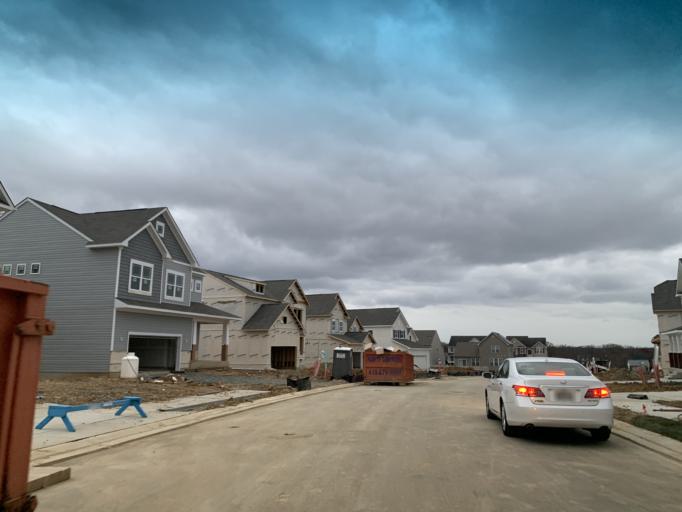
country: US
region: Maryland
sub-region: Harford County
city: Perryman
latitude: 39.4985
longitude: -76.2076
